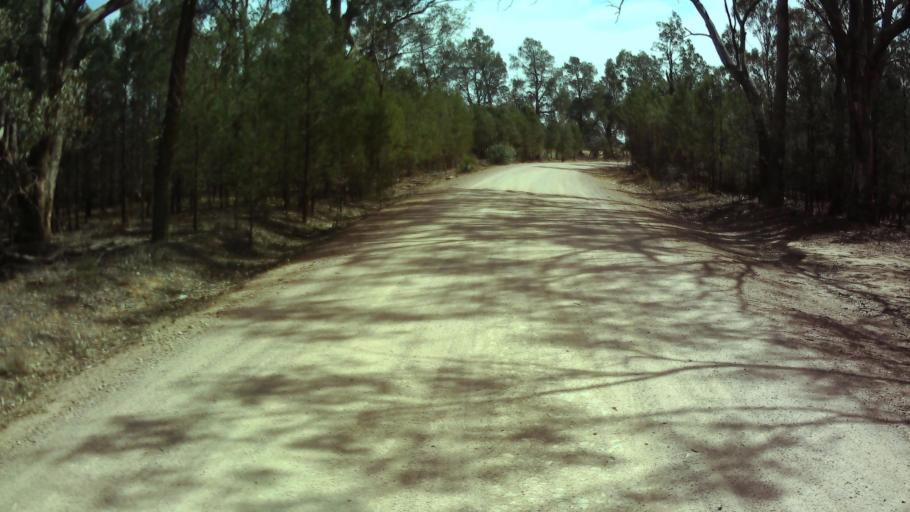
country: AU
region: New South Wales
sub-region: Weddin
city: Grenfell
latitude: -34.0355
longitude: 148.0829
